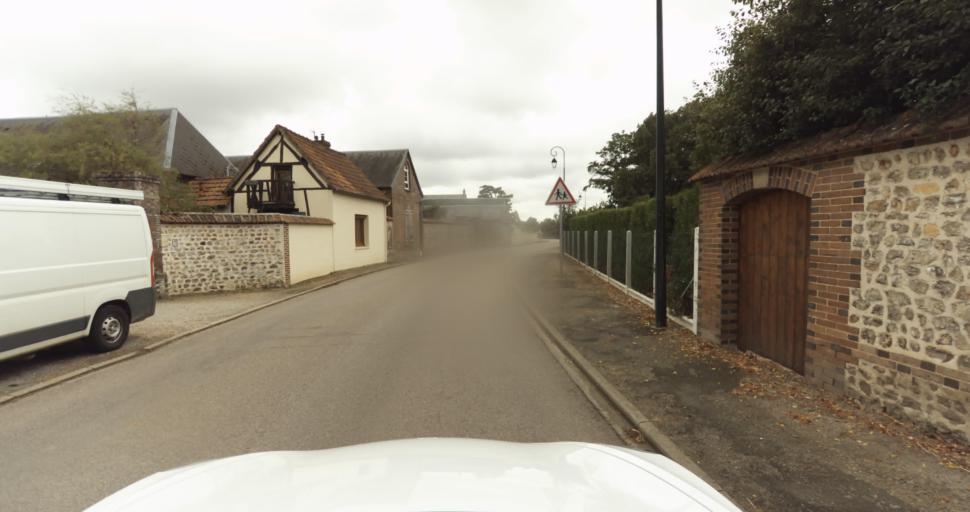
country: FR
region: Haute-Normandie
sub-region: Departement de l'Eure
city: Aviron
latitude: 49.0482
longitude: 1.0863
